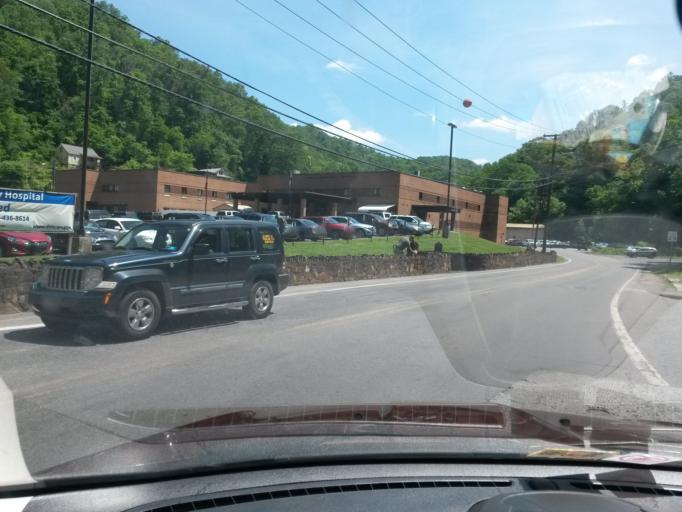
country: US
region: West Virginia
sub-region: McDowell County
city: Welch
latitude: 37.4385
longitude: -81.5891
